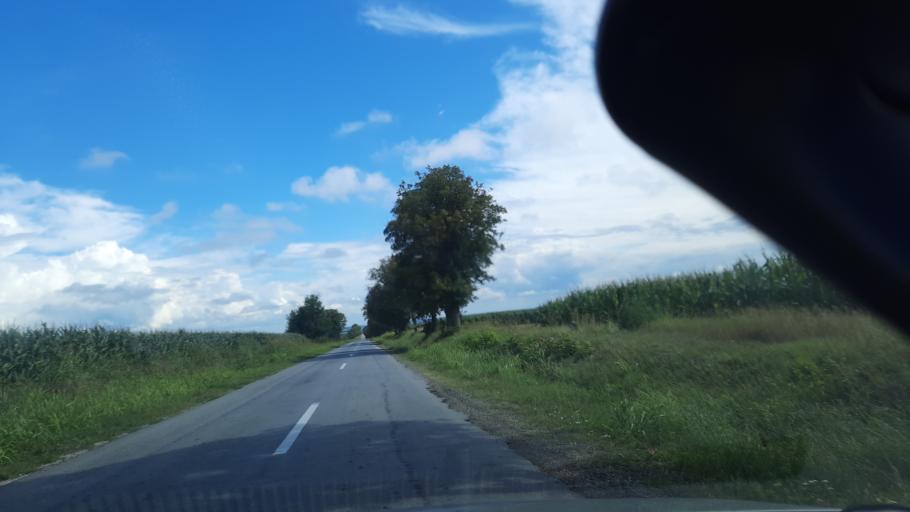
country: RS
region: Autonomna Pokrajina Vojvodina
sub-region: Sremski Okrug
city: Sremska Mitrovica
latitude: 45.0849
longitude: 19.5816
